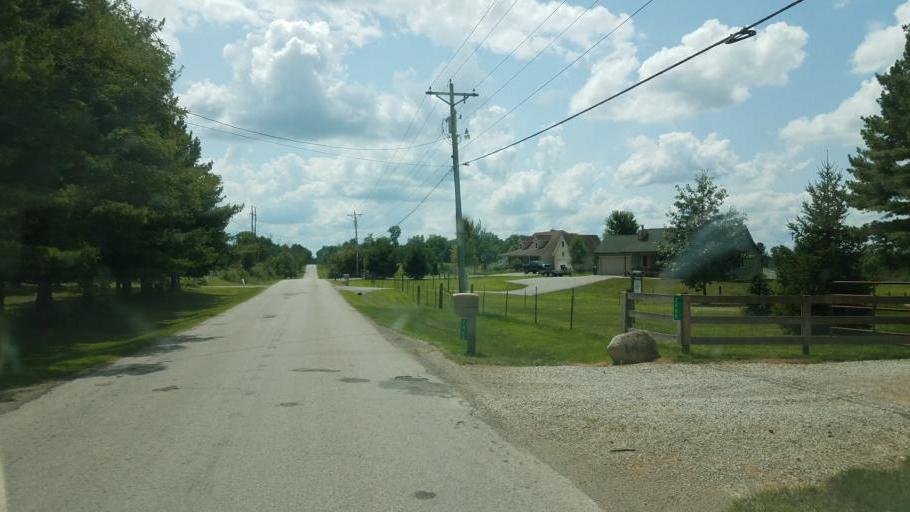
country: US
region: Ohio
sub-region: Morrow County
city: Mount Gilead
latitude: 40.4413
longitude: -82.7851
